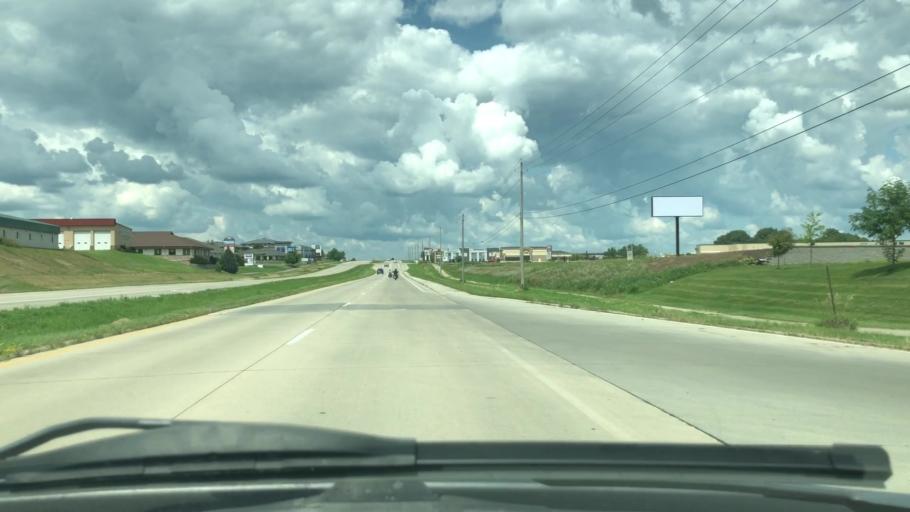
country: US
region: Minnesota
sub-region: Olmsted County
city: Rochester
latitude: 44.0469
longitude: -92.5208
